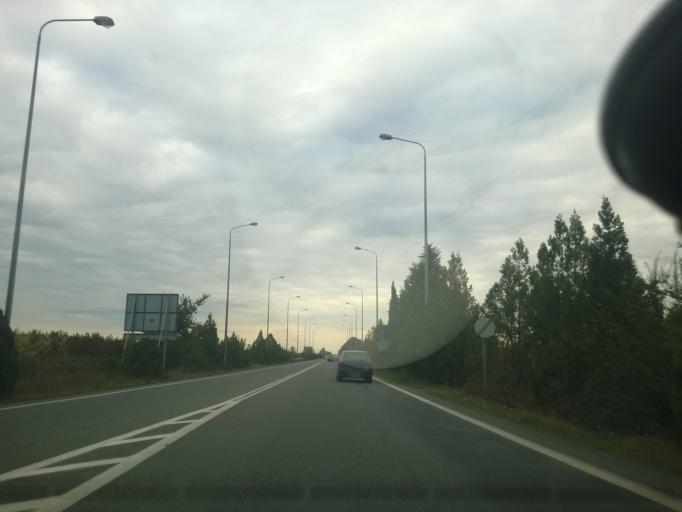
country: GR
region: Central Macedonia
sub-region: Nomos Pellis
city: Palaifyto
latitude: 40.7994
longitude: 22.2637
